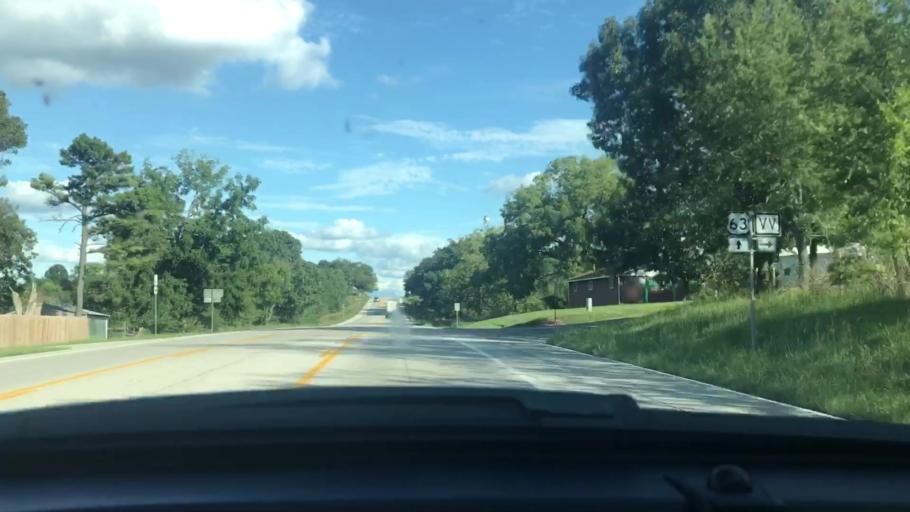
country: US
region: Missouri
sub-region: Howell County
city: West Plains
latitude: 36.6517
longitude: -91.6905
